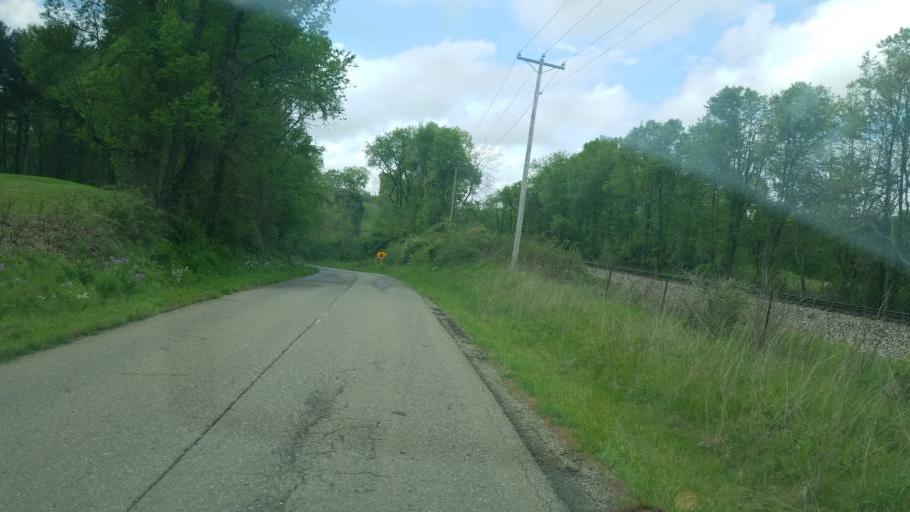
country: US
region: Ohio
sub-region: Tuscarawas County
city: Dover
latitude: 40.6043
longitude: -81.4255
